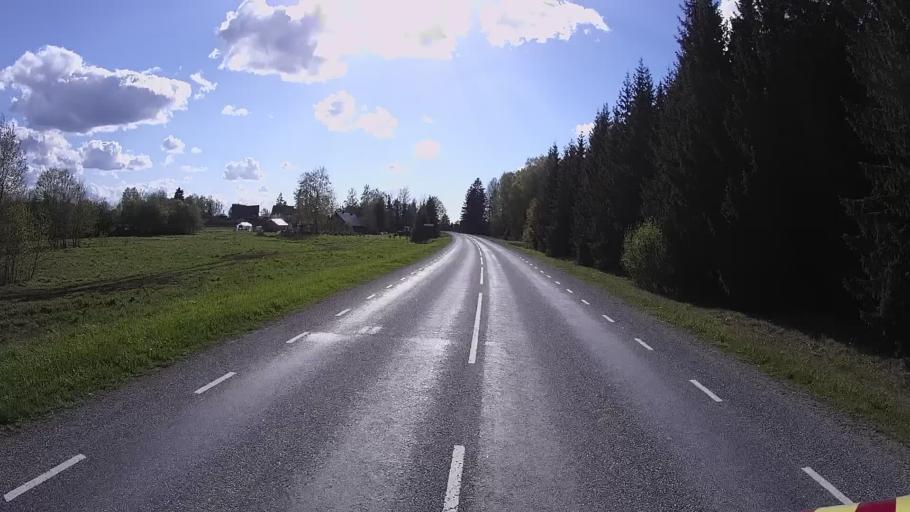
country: EE
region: Jogevamaa
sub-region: Poltsamaa linn
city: Poltsamaa
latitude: 58.6788
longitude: 26.0323
